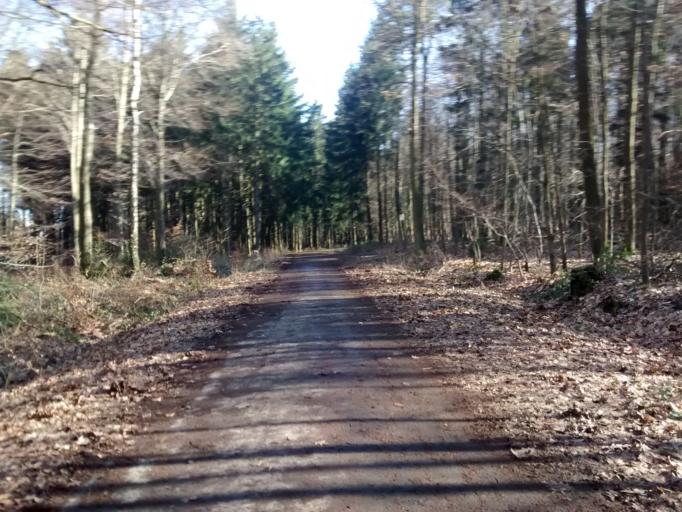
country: NL
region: Limburg
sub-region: Gemeente Vaals
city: Vaals
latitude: 50.7483
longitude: 6.0493
